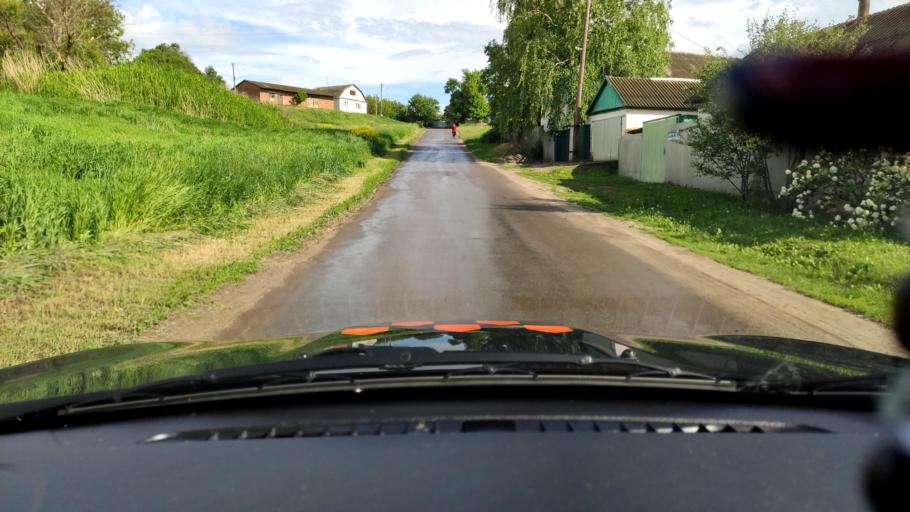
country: RU
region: Voronezj
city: Uryv-Pokrovka
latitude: 51.1102
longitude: 39.1639
